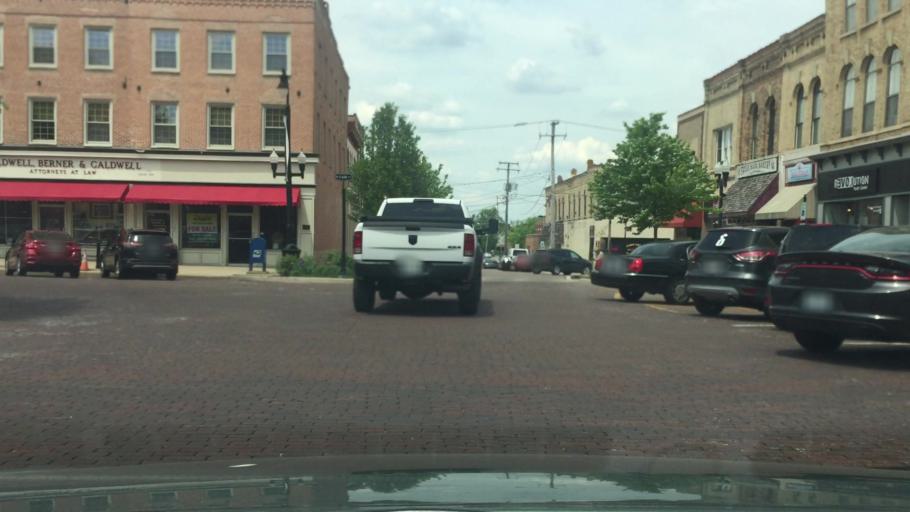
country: US
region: Illinois
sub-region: McHenry County
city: Woodstock
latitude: 42.3150
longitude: -88.4468
